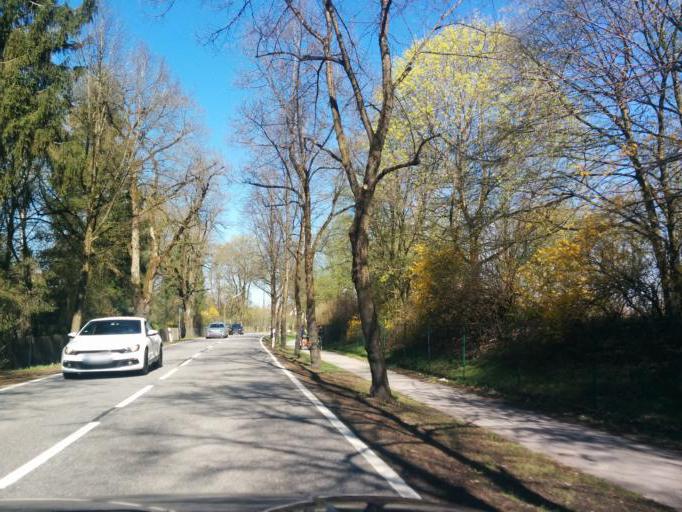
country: DE
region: Bavaria
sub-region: Upper Bavaria
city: Pullach im Isartal
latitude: 48.0810
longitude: 11.4998
